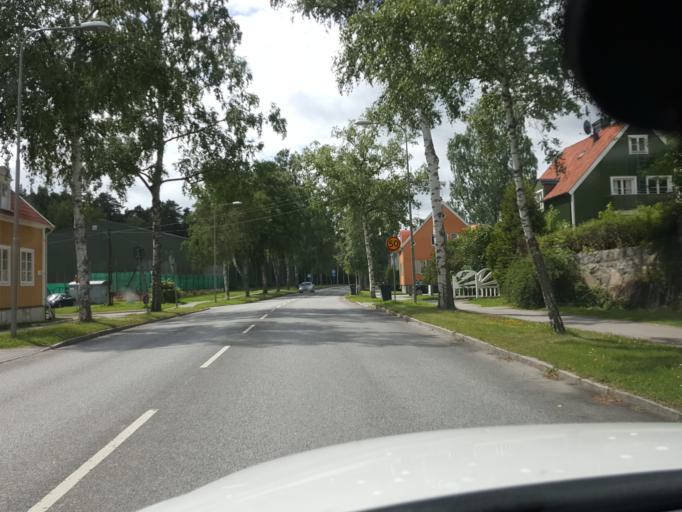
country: SE
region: Stockholm
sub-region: Stockholms Kommun
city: Bromma
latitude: 59.3185
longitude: 17.9657
